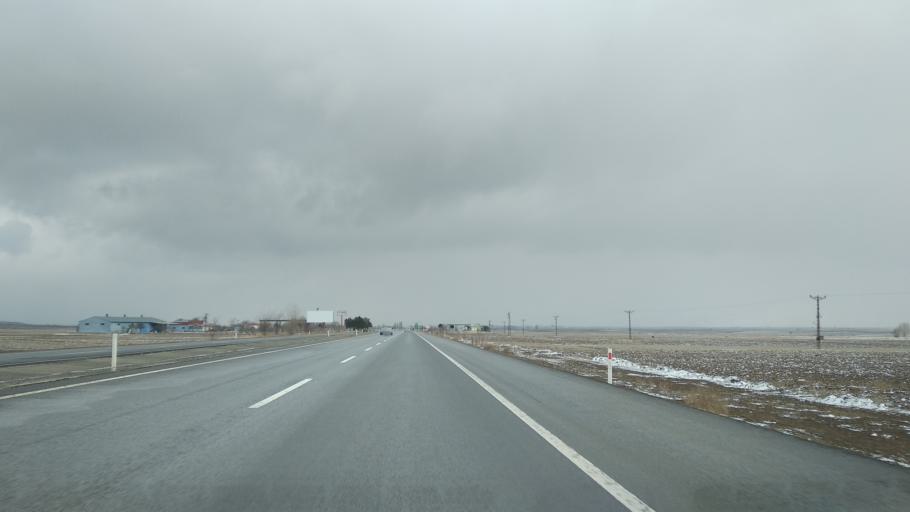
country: TR
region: Kayseri
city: Elbasi
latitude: 38.6397
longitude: 35.8918
